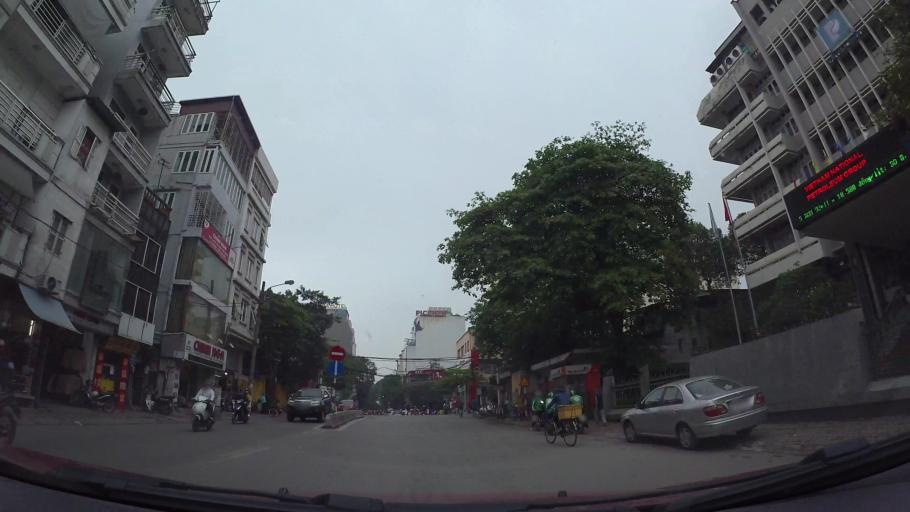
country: VN
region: Ha Noi
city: Hanoi
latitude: 21.0189
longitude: 105.8403
